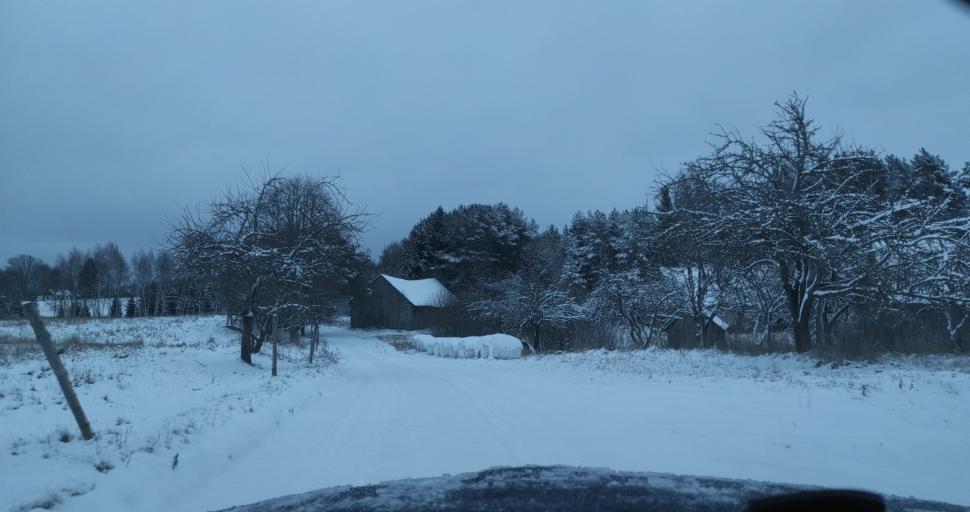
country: LV
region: Alsunga
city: Alsunga
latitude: 56.9563
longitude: 21.6159
